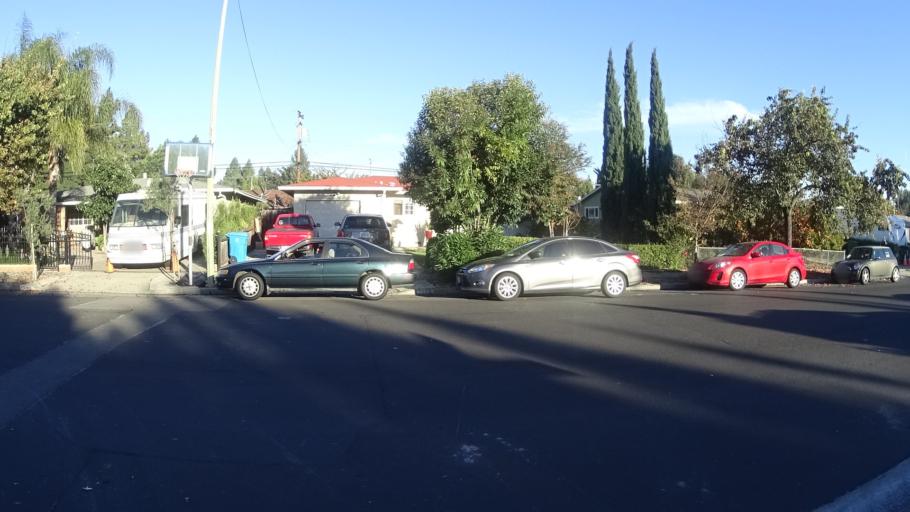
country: US
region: California
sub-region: Santa Clara County
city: Santa Clara
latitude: 37.3684
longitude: -121.9778
